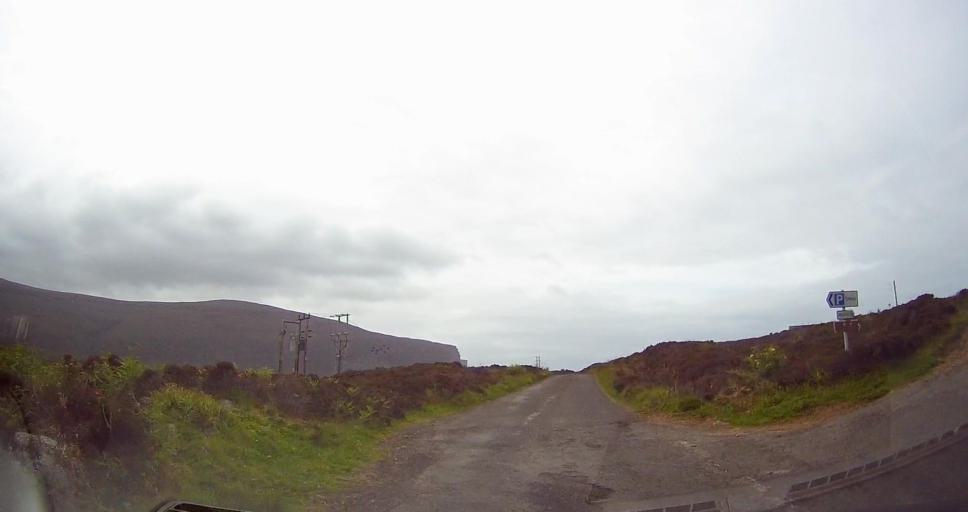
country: GB
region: Scotland
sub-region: Orkney Islands
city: Stromness
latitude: 58.8791
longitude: -3.3860
